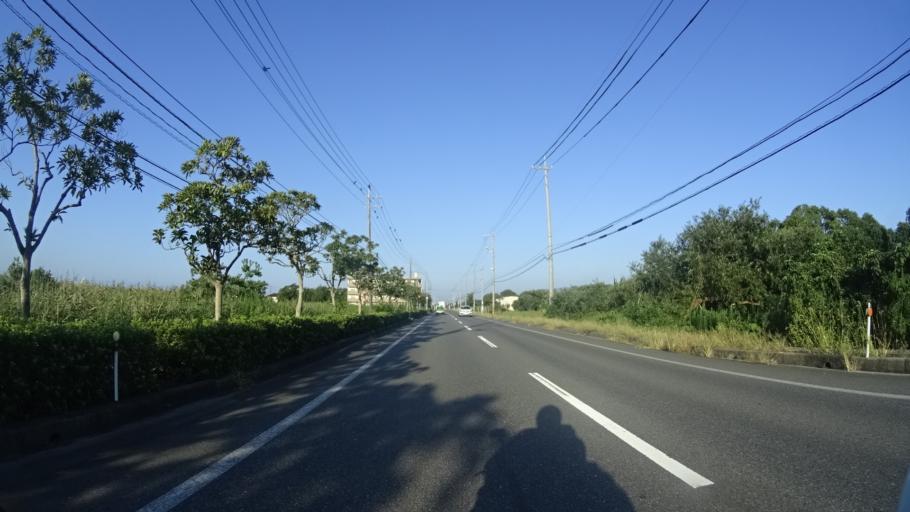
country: JP
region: Shimane
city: Sakaiminato
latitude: 35.5211
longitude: 133.2269
